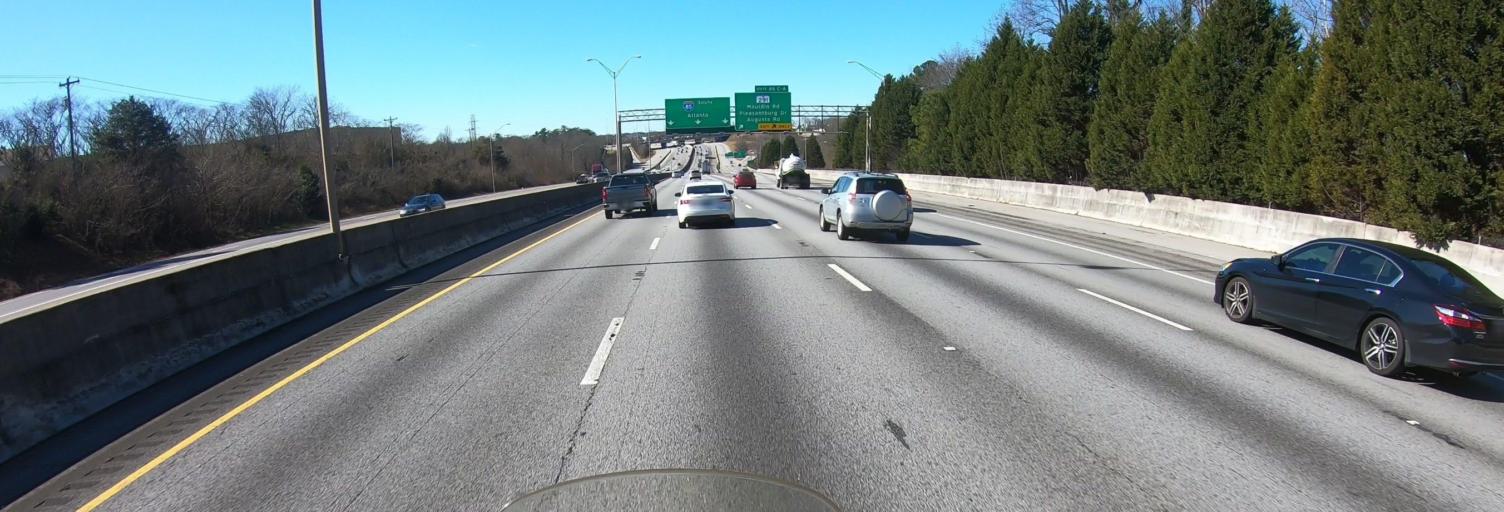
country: US
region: South Carolina
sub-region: Greenville County
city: Mauldin
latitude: 34.8021
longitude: -82.3603
